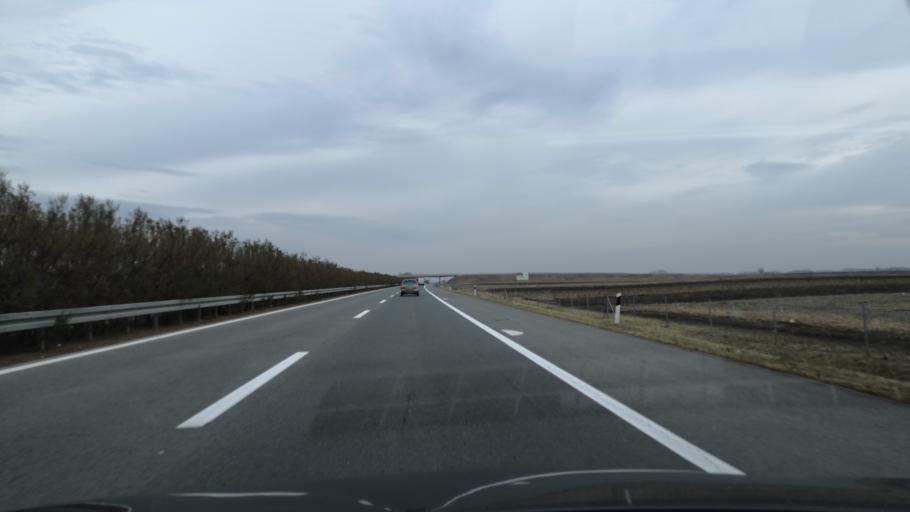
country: RS
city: Kisac
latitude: 45.3564
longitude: 19.7559
